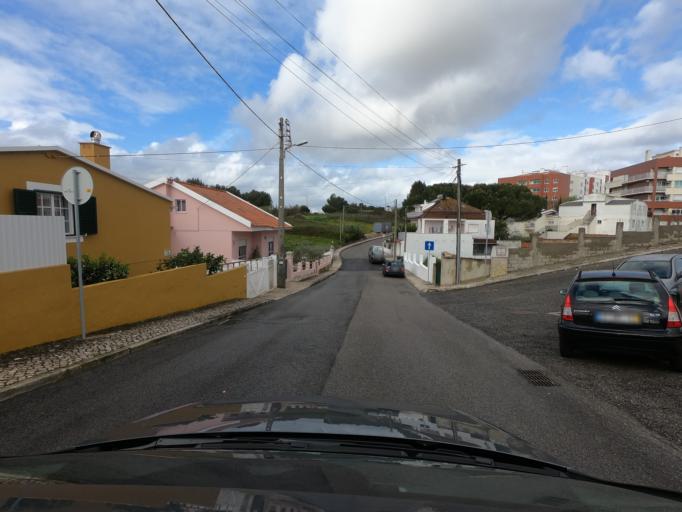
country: PT
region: Lisbon
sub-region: Cascais
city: Sao Domingos de Rana
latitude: 38.7090
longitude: -9.3260
